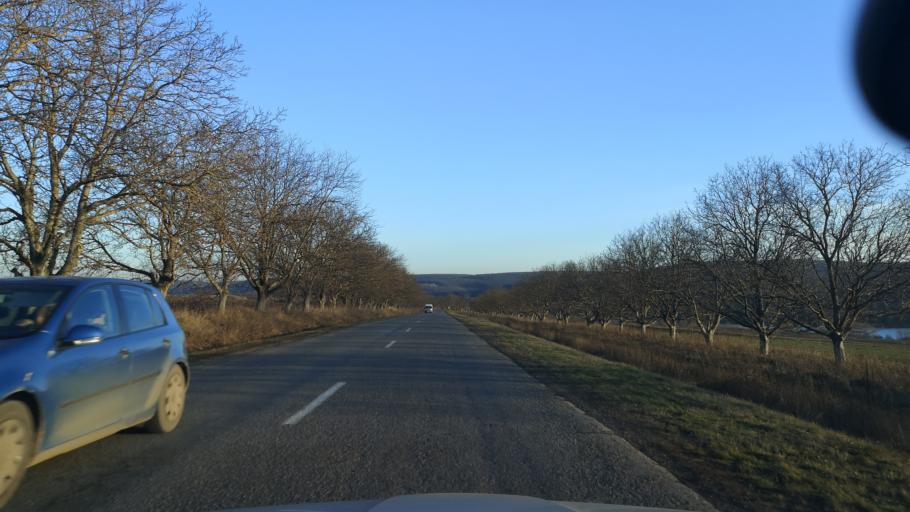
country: MD
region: Orhei
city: Orhei
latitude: 47.2872
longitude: 28.8221
